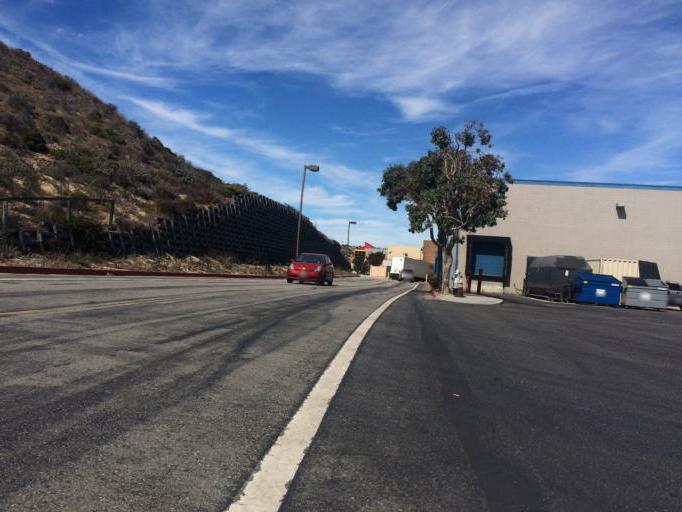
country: US
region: California
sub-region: Monterey County
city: Seaside
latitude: 36.6182
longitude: -121.8466
